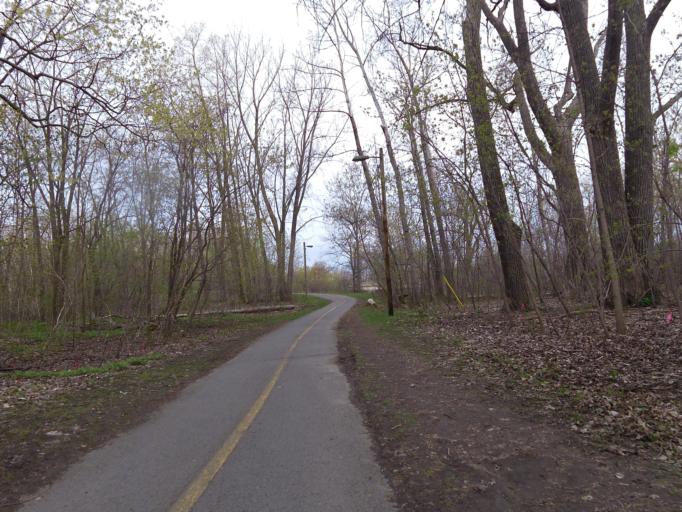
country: CA
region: Quebec
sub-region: Laval
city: Laval
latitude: 45.5468
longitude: -73.6962
